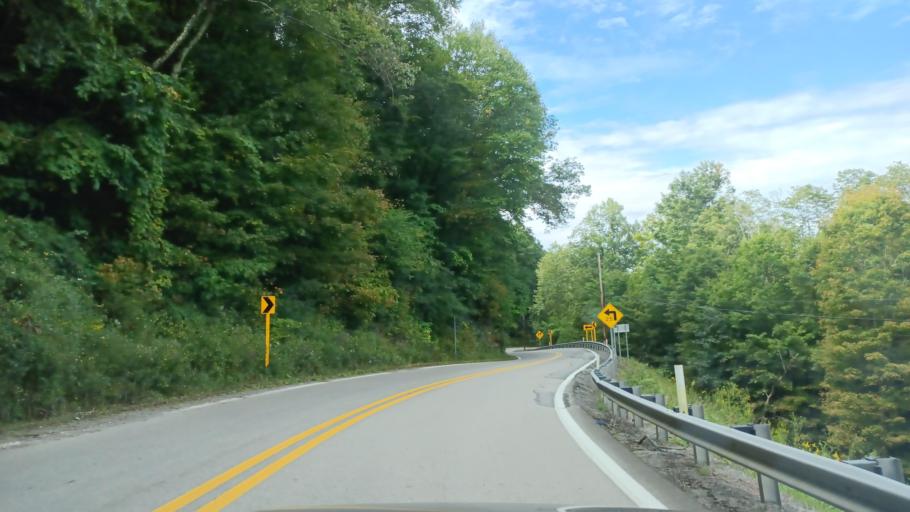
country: US
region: West Virginia
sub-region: Preston County
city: Terra Alta
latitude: 39.3016
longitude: -79.5990
